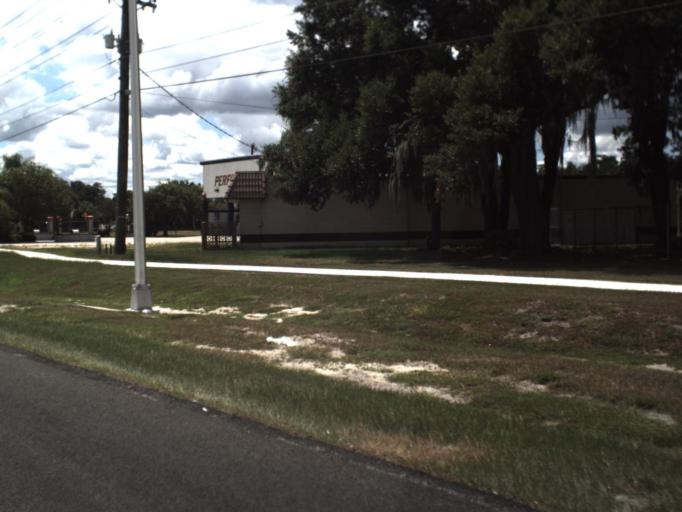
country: US
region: Florida
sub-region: Polk County
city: Highland City
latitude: 27.9958
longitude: -81.8989
